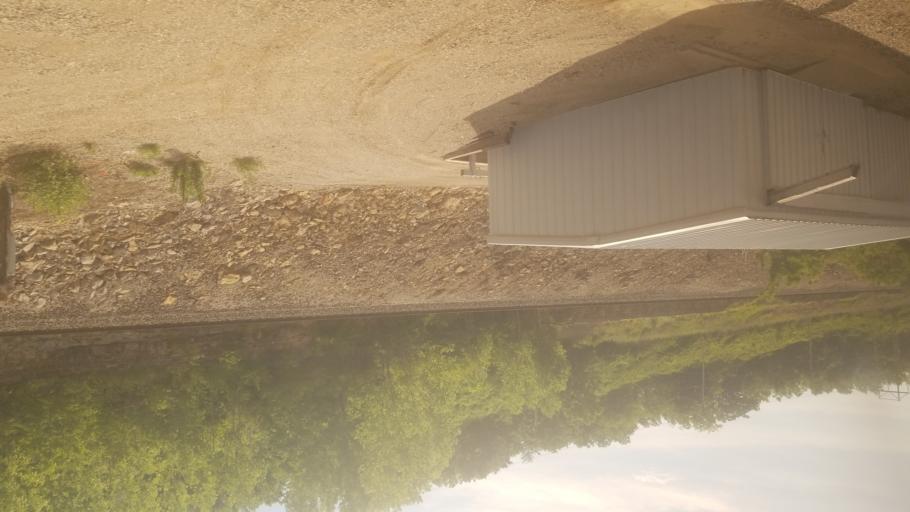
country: US
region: Kansas
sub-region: Johnson County
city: Westwood
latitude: 39.0768
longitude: -94.6178
